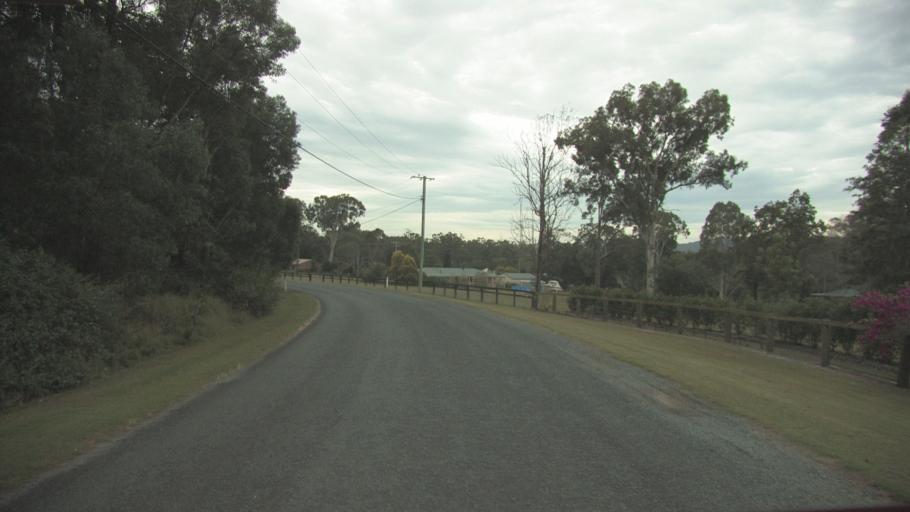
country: AU
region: Queensland
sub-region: Logan
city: Chambers Flat
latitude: -27.7886
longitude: 153.1118
